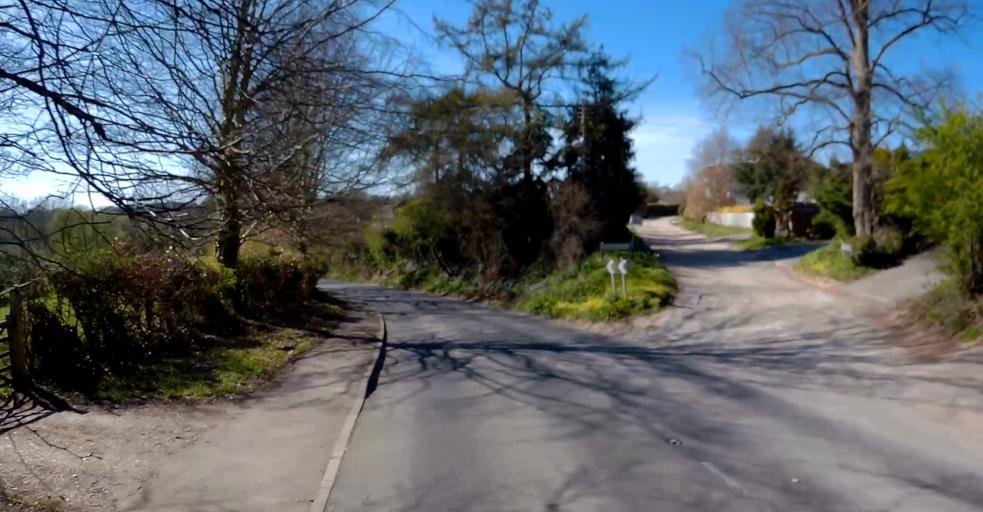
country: GB
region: England
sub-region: Surrey
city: Farnham
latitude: 51.2155
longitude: -0.8180
